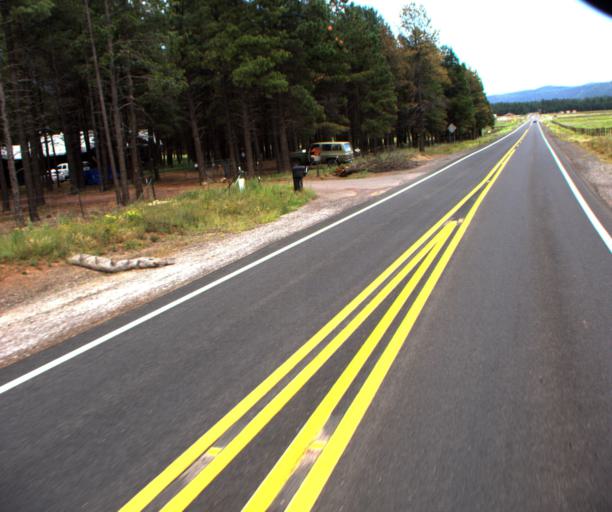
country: US
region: Arizona
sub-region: Coconino County
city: Flagstaff
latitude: 35.2680
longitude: -111.7348
